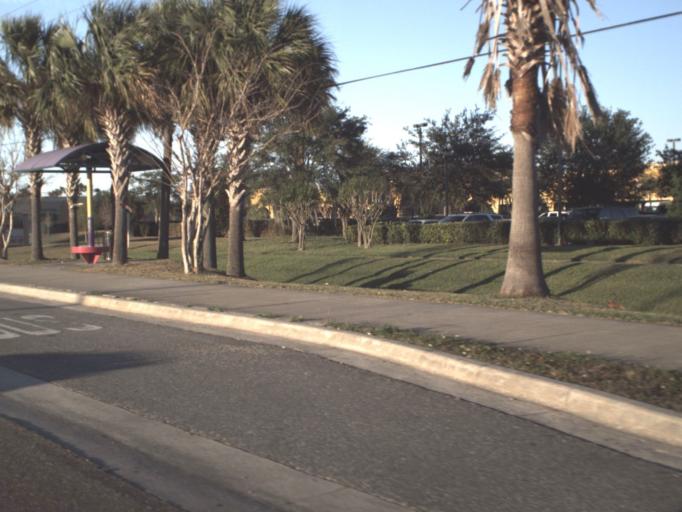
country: US
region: Florida
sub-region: Orange County
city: Conway
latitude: 28.4663
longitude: -81.3099
